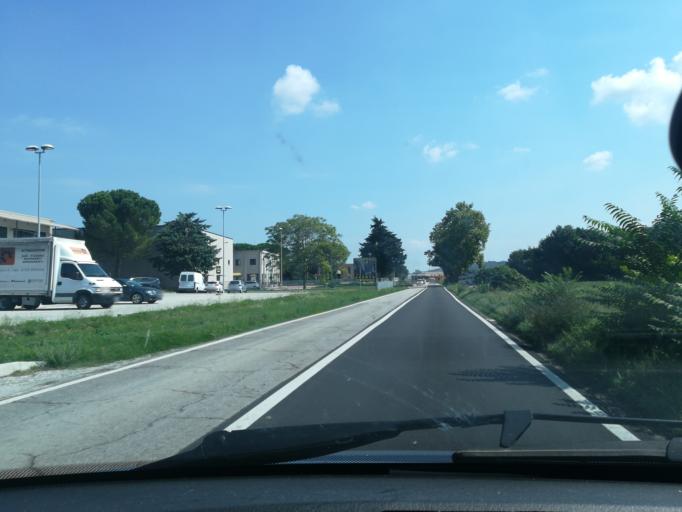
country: IT
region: The Marches
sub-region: Provincia di Macerata
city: Tolentino
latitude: 43.2210
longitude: 13.3259
